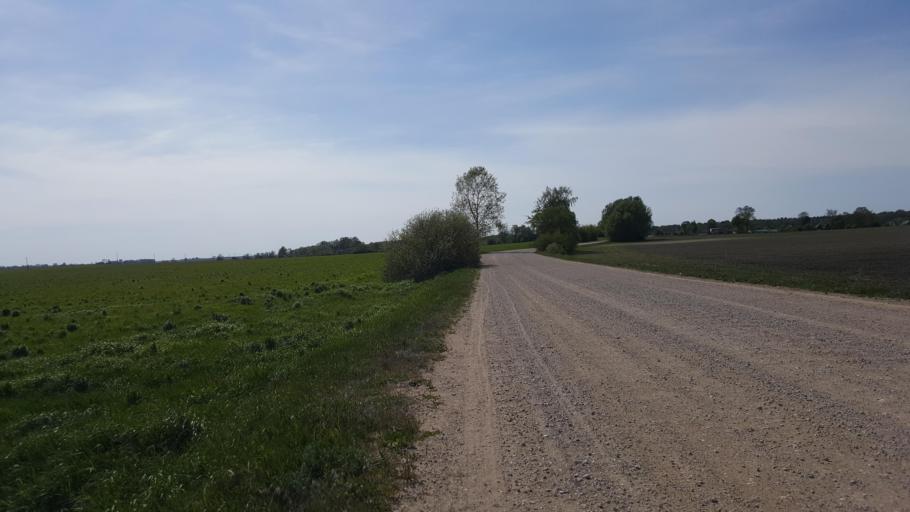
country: BY
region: Brest
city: Zhabinka
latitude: 52.3137
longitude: 24.0510
